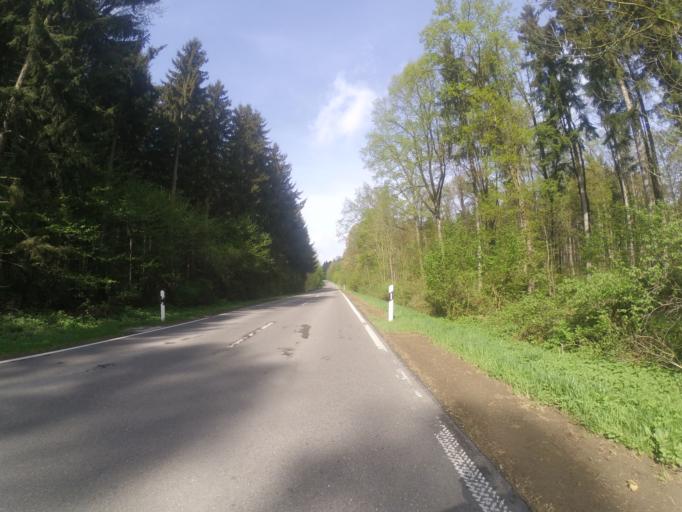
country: DE
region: Baden-Wuerttemberg
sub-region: Tuebingen Region
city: Griesingen
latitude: 48.2428
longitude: 9.8046
